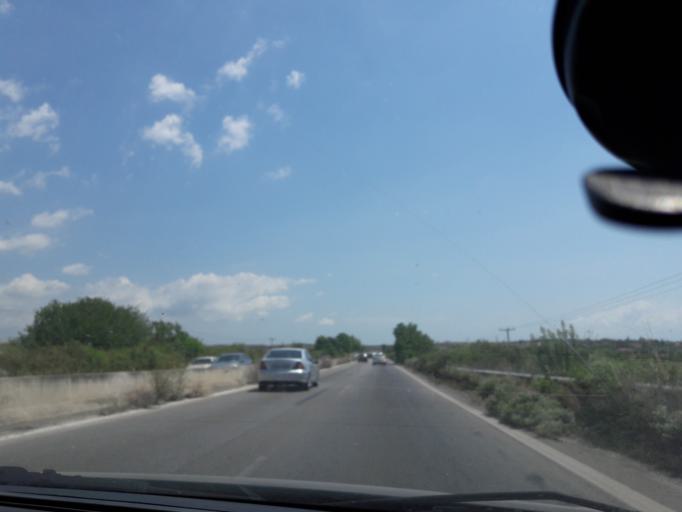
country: GR
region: Central Macedonia
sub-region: Nomos Chalkidikis
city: Nea Kallikrateia
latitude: 40.3101
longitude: 23.1177
